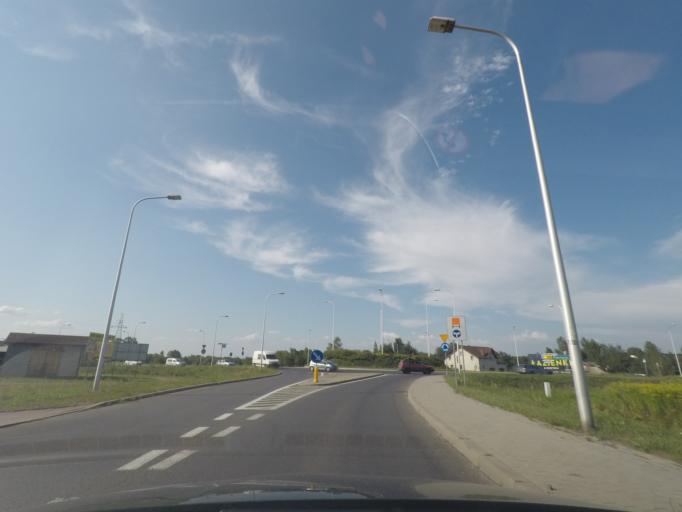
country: PL
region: Silesian Voivodeship
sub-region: Zory
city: Zory
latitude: 50.0580
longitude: 18.6826
